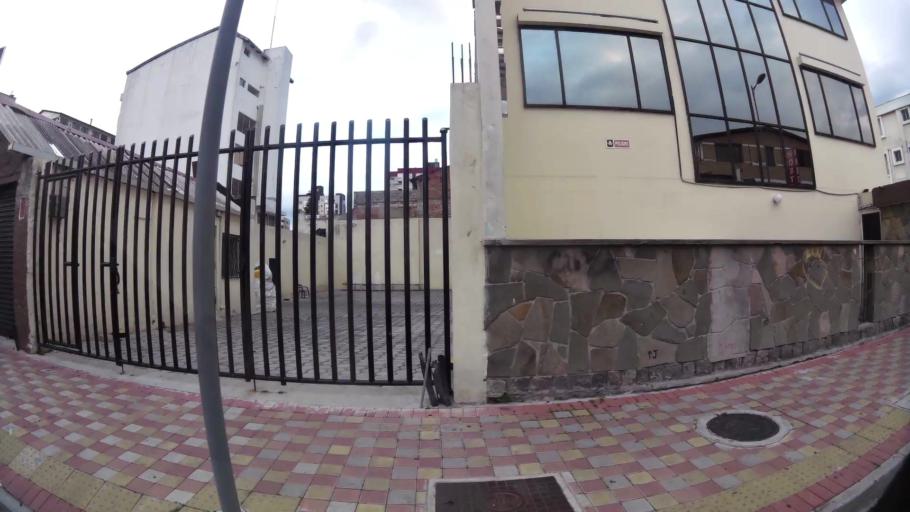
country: EC
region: Pichincha
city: Quito
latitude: -0.2045
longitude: -78.4911
